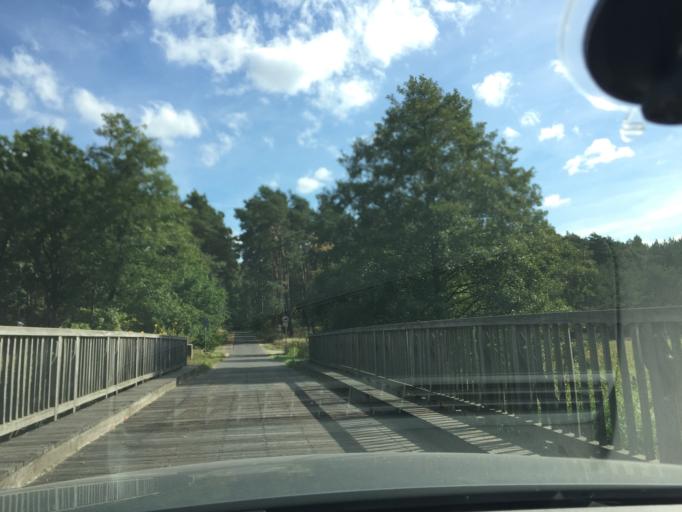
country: DE
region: Brandenburg
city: Spreenhagen
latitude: 52.3838
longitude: 13.8917
